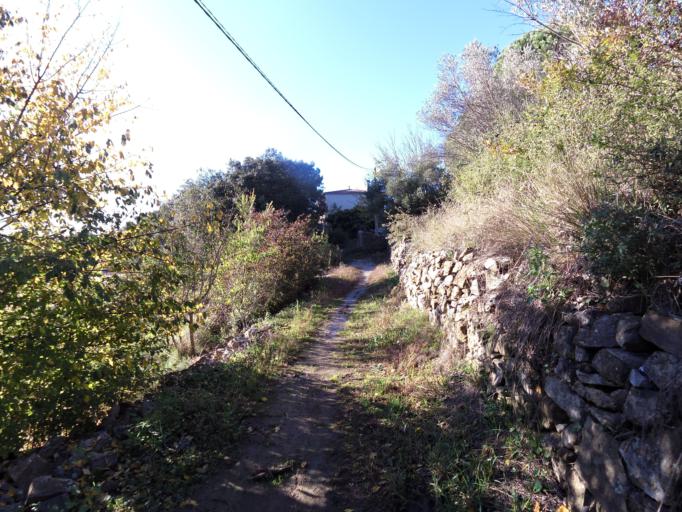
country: FR
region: Languedoc-Roussillon
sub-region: Departement du Gard
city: Sauve
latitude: 43.9921
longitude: 3.9520
